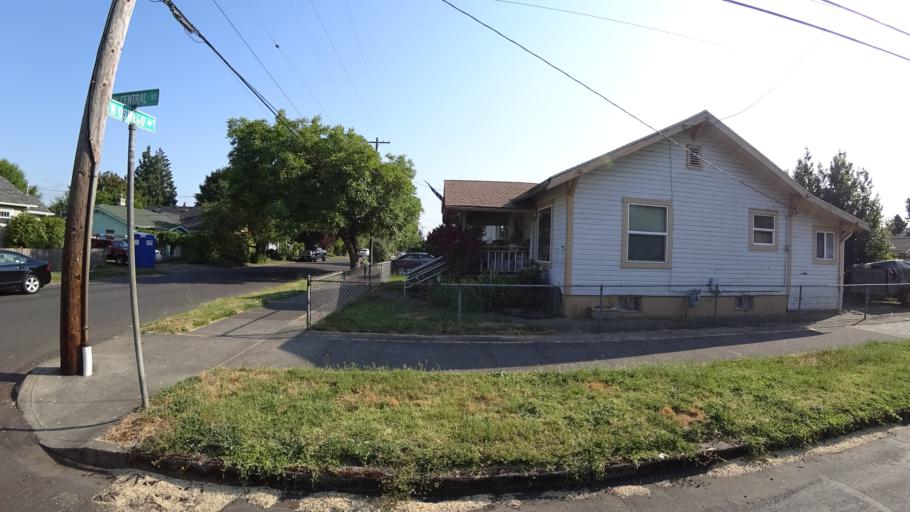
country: US
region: Oregon
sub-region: Washington County
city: West Haven
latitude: 45.5908
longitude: -122.7485
